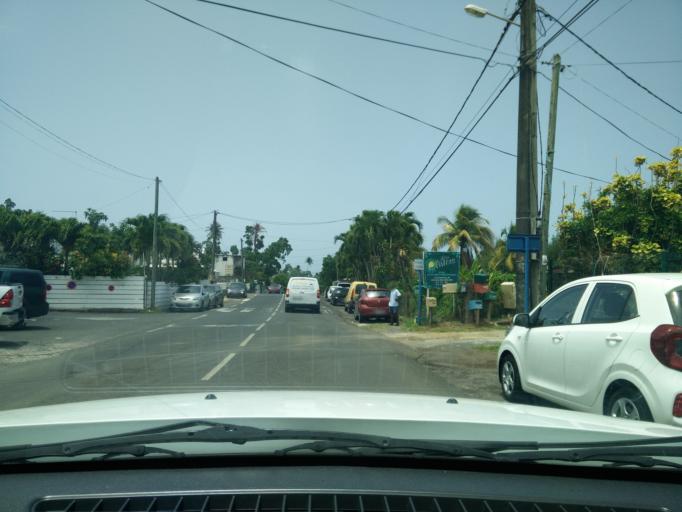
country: GP
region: Guadeloupe
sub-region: Guadeloupe
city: Trois-Rivieres
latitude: 15.9773
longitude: -61.6382
